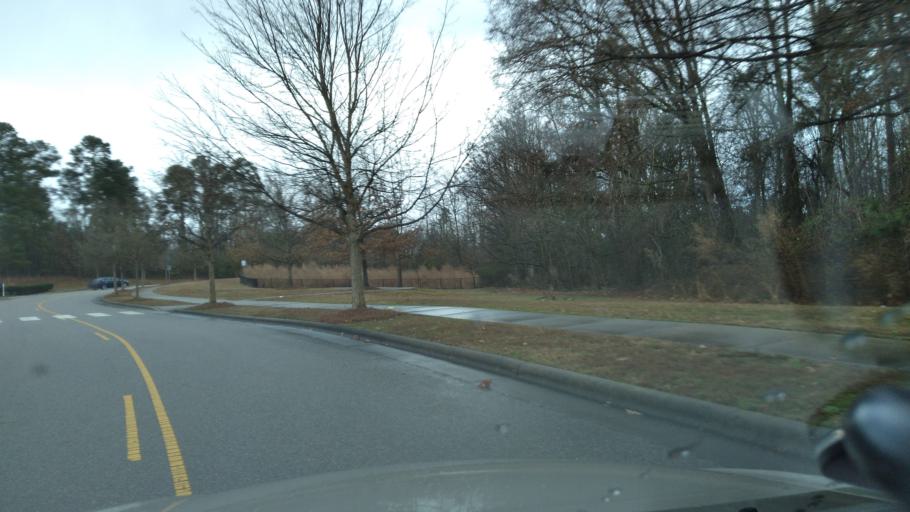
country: US
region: North Carolina
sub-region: Wake County
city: Knightdale
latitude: 35.7979
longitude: -78.5184
